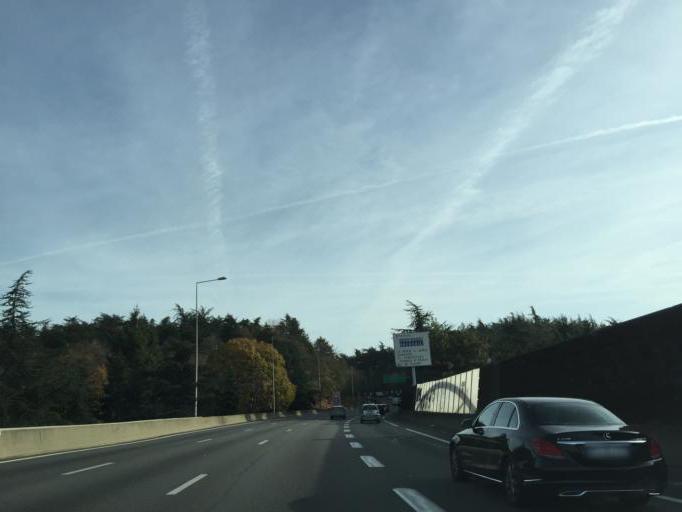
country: FR
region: Rhone-Alpes
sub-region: Departement du Rhone
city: Bron
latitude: 45.7238
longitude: 4.8920
